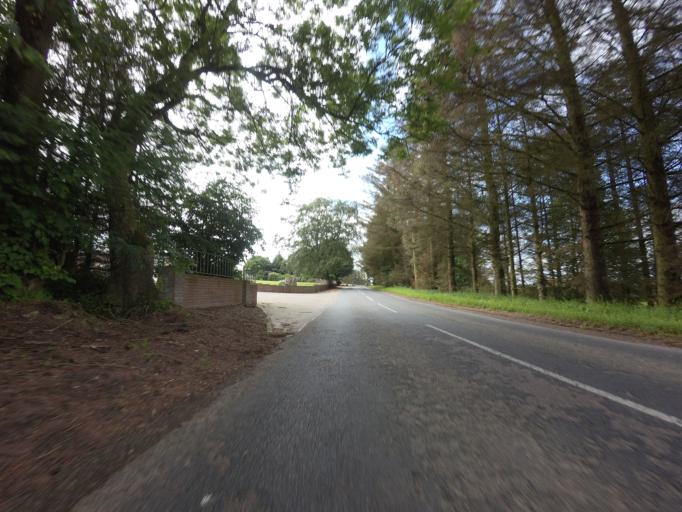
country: GB
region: Scotland
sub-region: Aberdeenshire
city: Turriff
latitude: 57.5429
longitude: -2.3150
